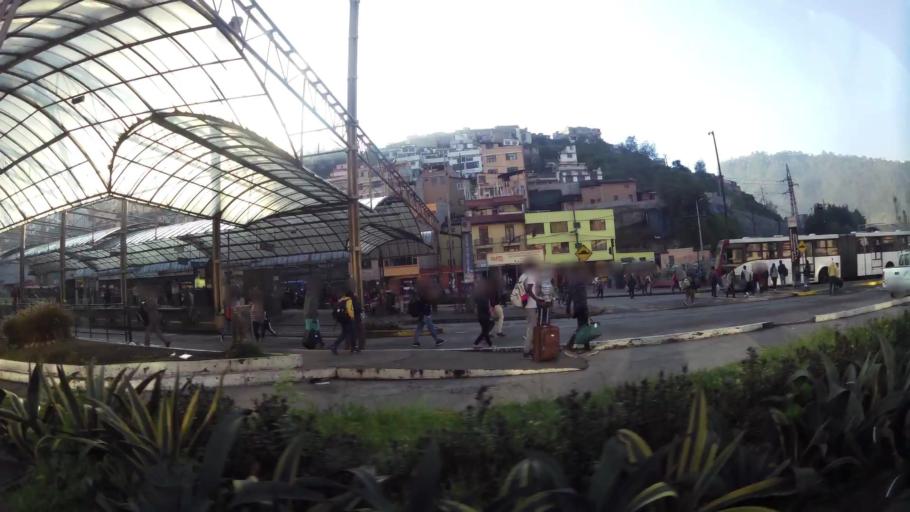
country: EC
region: Pichincha
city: Quito
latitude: -0.2284
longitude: -78.5071
